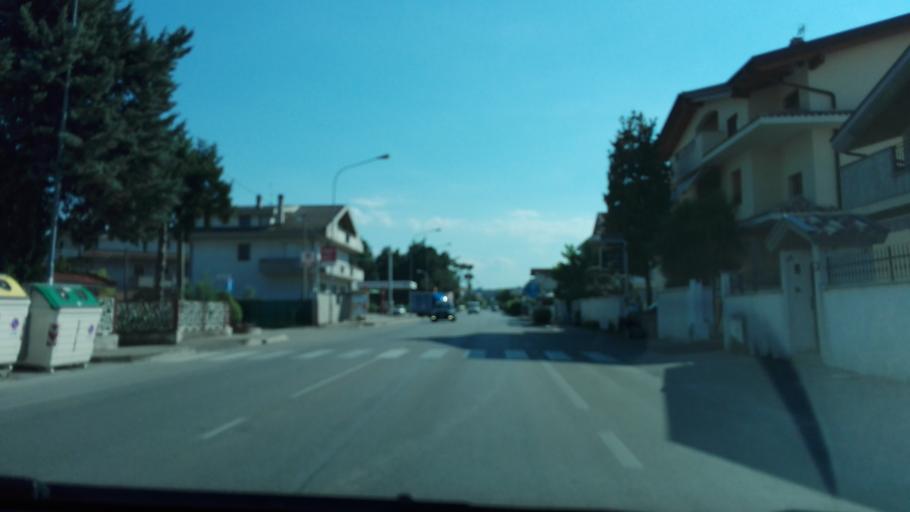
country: IT
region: Abruzzo
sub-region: Provincia di Pescara
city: Cappelle sul Tavo
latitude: 42.4891
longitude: 14.1214
